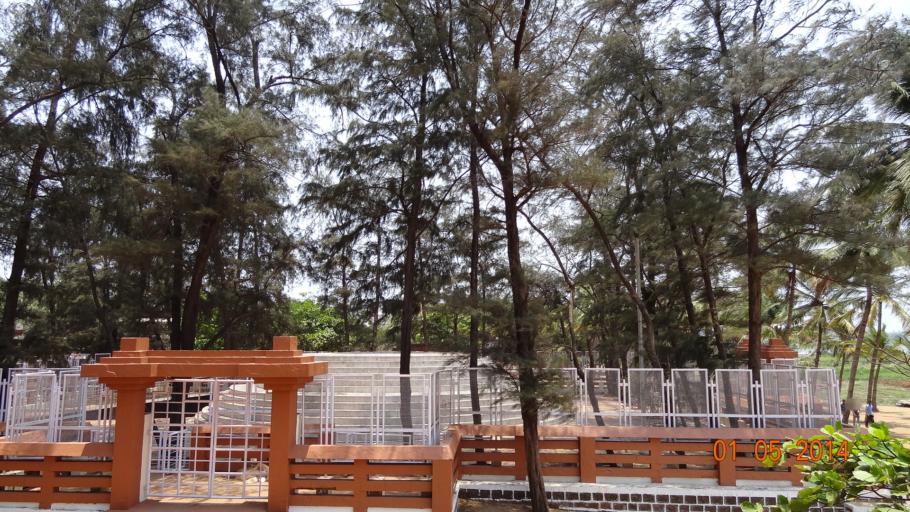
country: IN
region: Goa
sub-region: North Goa
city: Panaji
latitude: 15.4826
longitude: 73.8085
